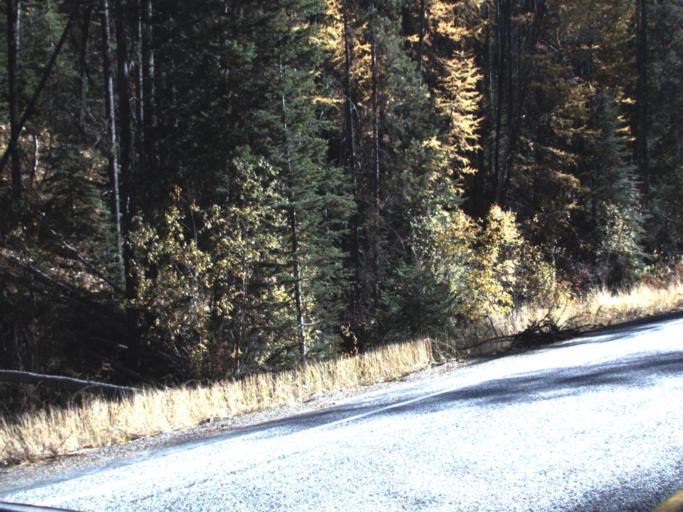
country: US
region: Washington
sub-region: Ferry County
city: Republic
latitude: 48.6229
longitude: -118.4344
